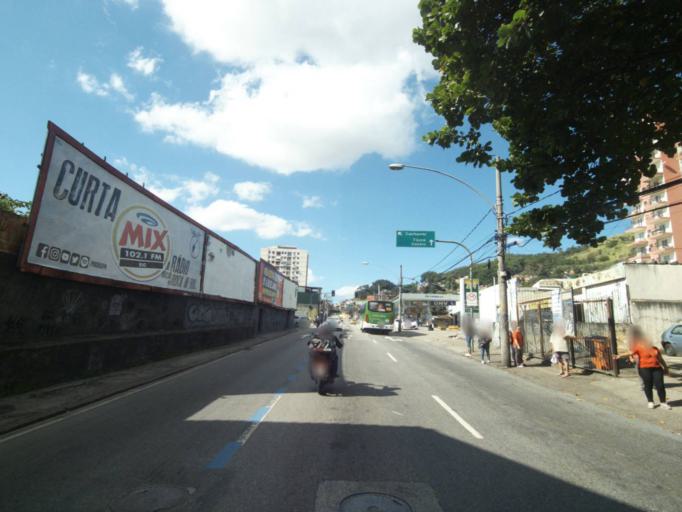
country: BR
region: Rio de Janeiro
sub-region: Rio De Janeiro
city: Rio de Janeiro
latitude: -22.9050
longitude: -43.2680
